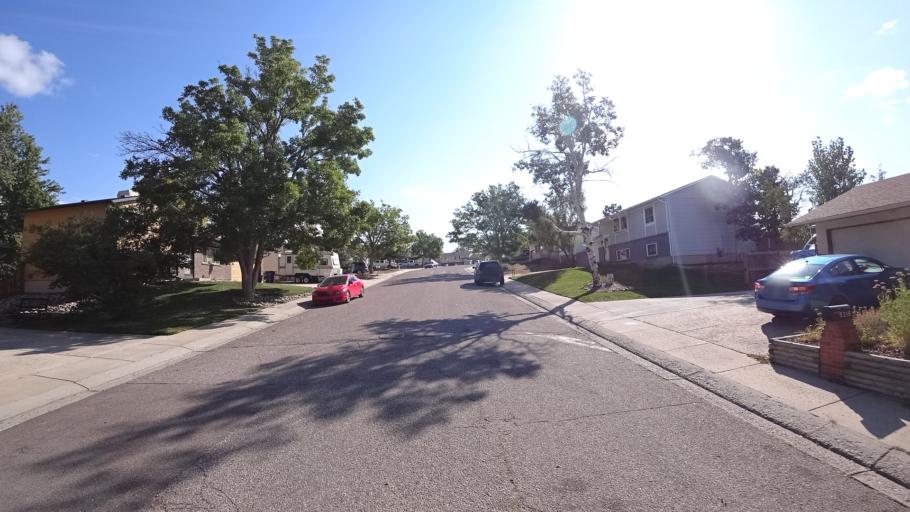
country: US
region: Colorado
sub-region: El Paso County
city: Cimarron Hills
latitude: 38.8820
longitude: -104.7311
